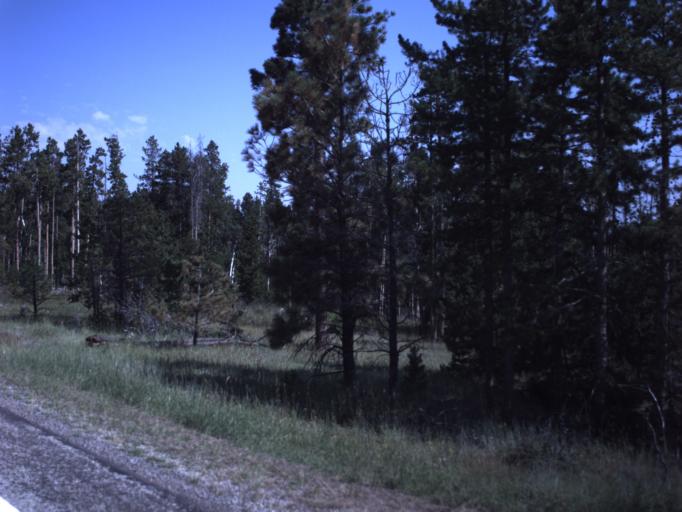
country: US
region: Utah
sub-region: Daggett County
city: Manila
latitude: 40.8511
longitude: -109.5889
